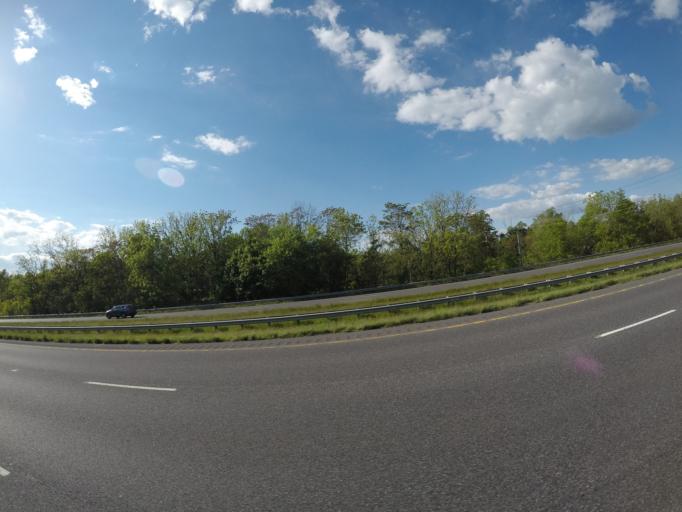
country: US
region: Maryland
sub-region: Carroll County
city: Mount Airy
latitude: 39.3600
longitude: -77.1501
